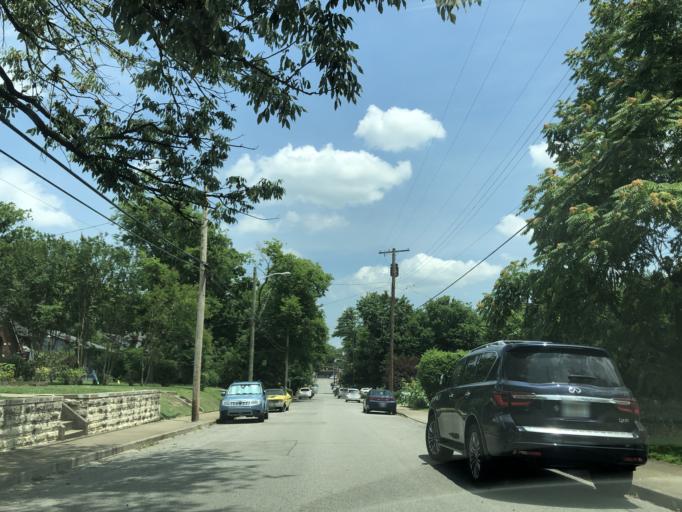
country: US
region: Tennessee
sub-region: Davidson County
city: Nashville
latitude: 36.1817
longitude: -86.7532
